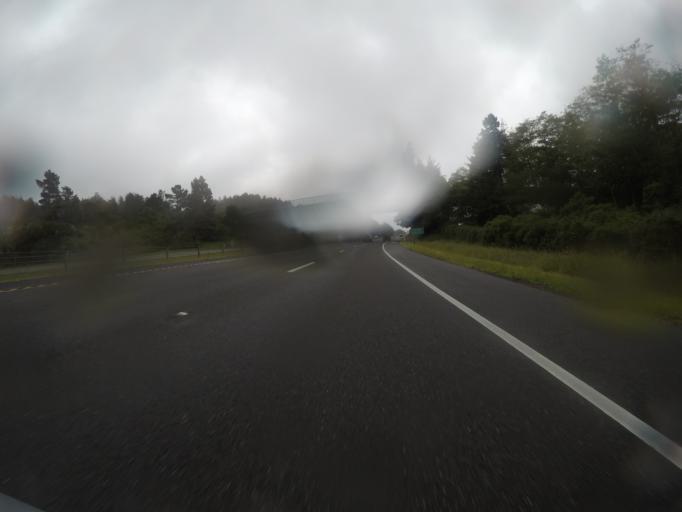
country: US
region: California
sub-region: Humboldt County
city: Arcata
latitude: 40.8870
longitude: -124.0799
